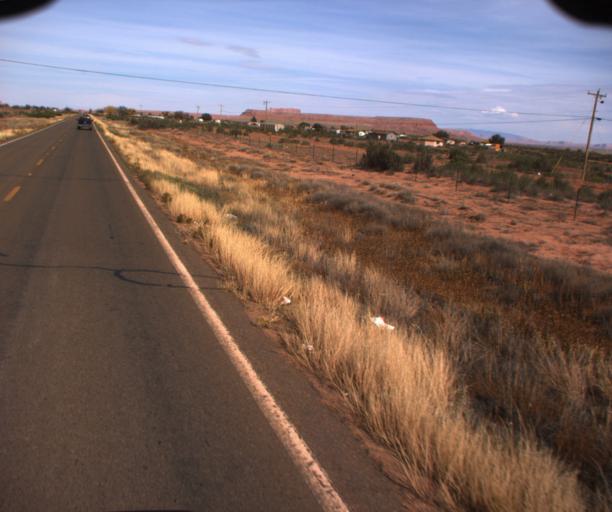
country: US
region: Arizona
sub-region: Apache County
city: Many Farms
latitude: 36.4015
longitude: -109.6088
